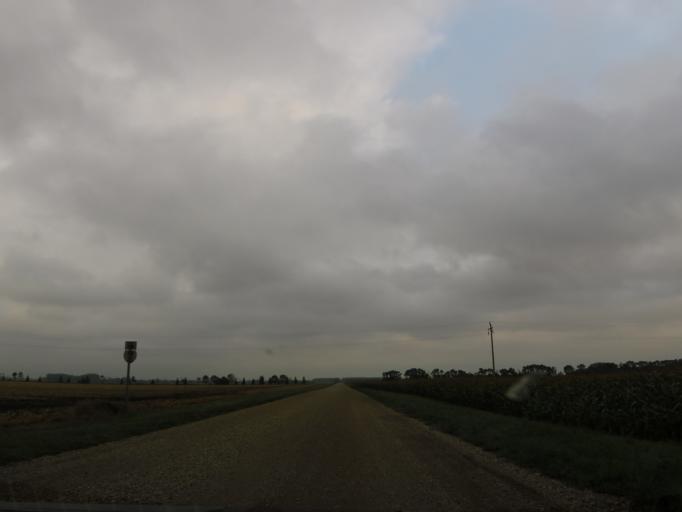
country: US
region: North Dakota
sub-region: Walsh County
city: Grafton
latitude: 48.4705
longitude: -97.1865
